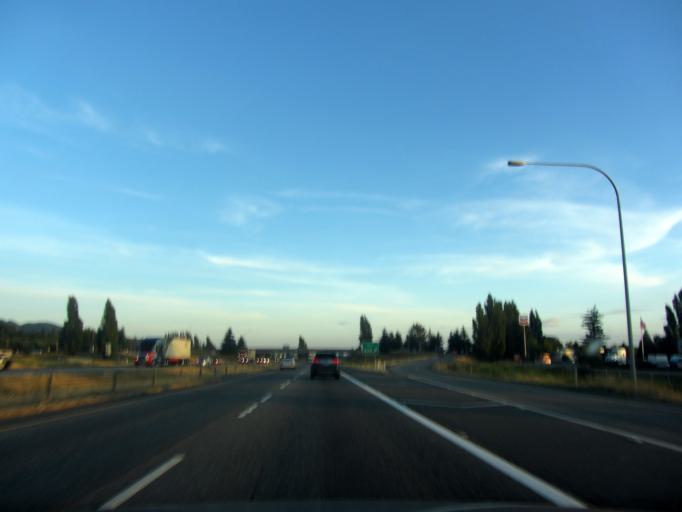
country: US
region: Washington
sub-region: Skagit County
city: Mount Vernon
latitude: 48.4023
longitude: -122.3308
